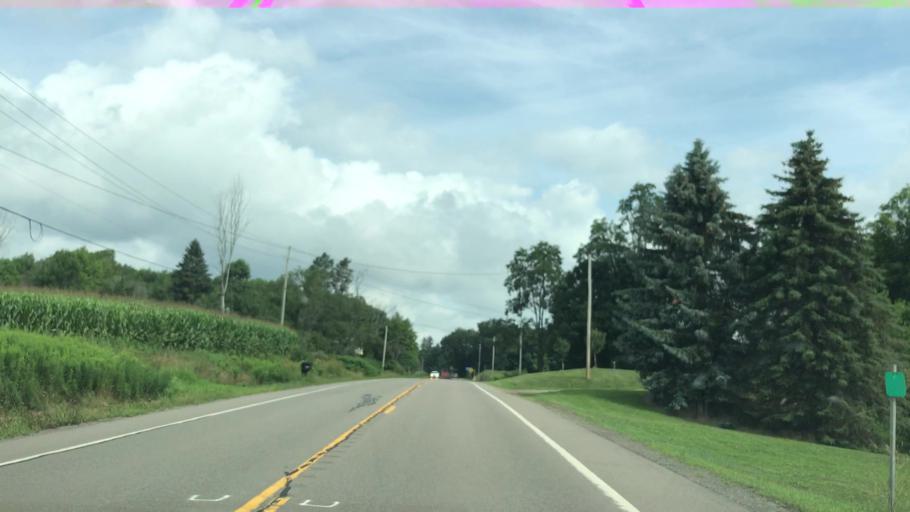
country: US
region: New York
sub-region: Ontario County
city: Naples
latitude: 42.5045
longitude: -77.2858
